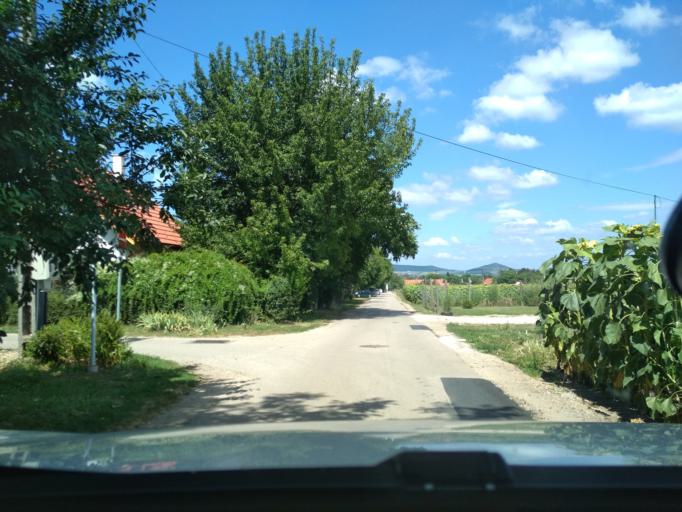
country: HU
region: Fejer
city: Velence
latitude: 47.2147
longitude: 18.6625
